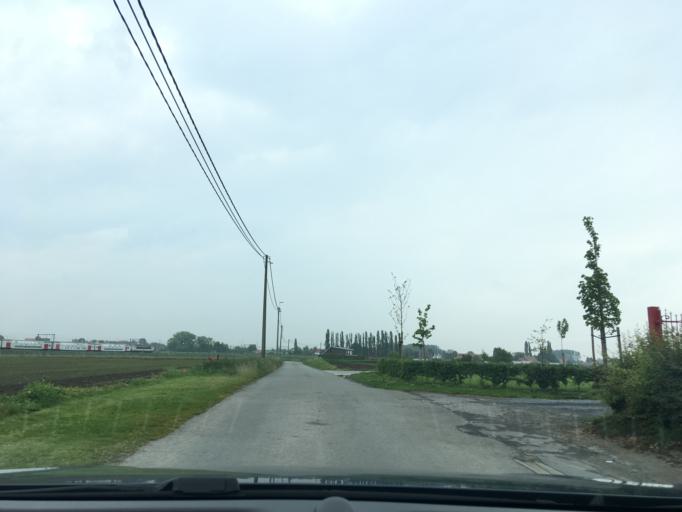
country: BE
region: Flanders
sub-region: Provincie West-Vlaanderen
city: Lichtervelde
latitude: 51.0113
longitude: 3.1245
